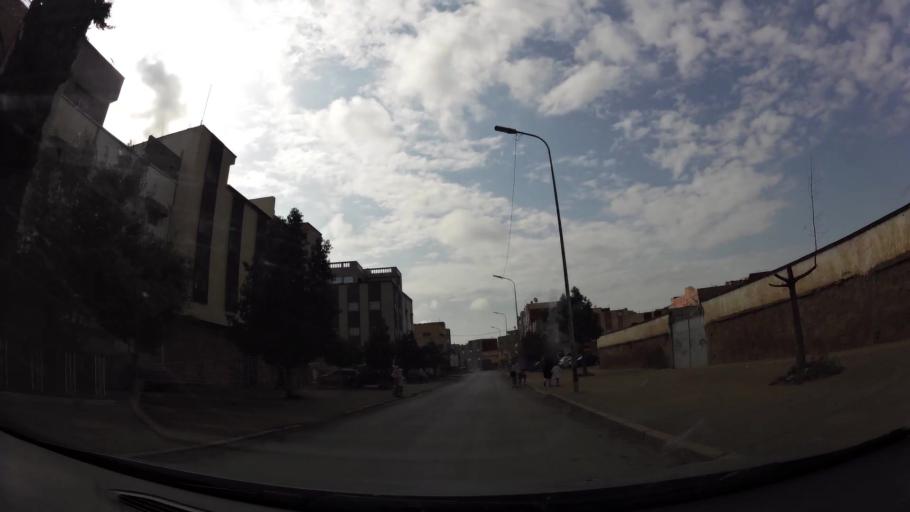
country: MA
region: Rabat-Sale-Zemmour-Zaer
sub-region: Khemisset
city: Tiflet
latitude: 33.8866
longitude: -6.3156
